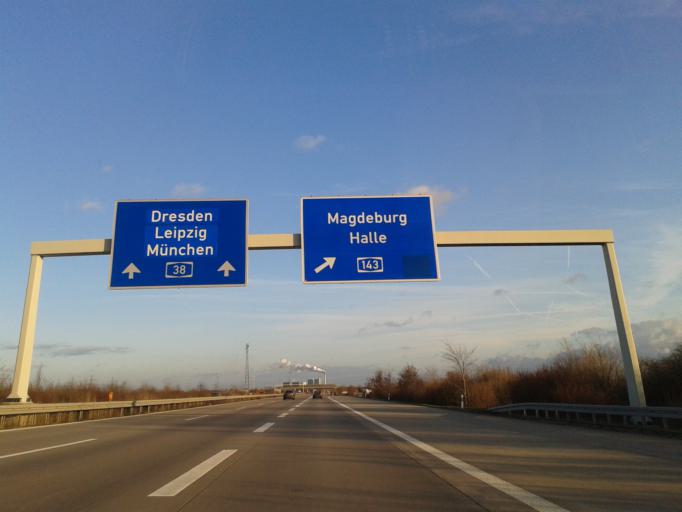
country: DE
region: Saxony-Anhalt
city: Bad Lauchstadt
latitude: 51.4038
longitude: 11.8590
